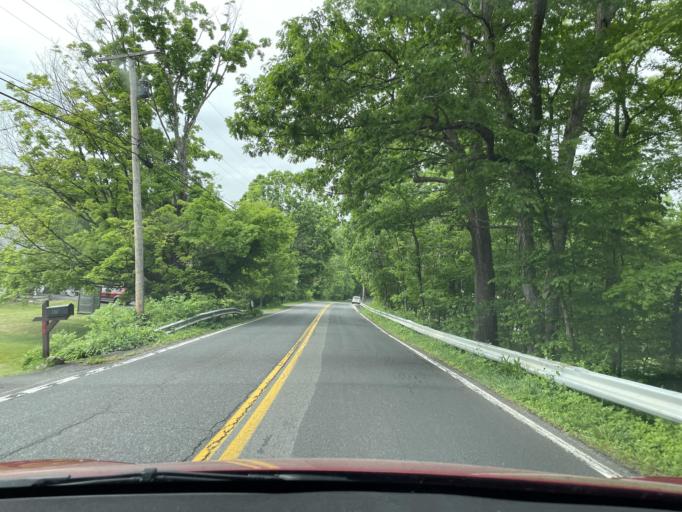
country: US
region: New York
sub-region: Ulster County
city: Zena
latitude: 41.9986
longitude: -74.0820
